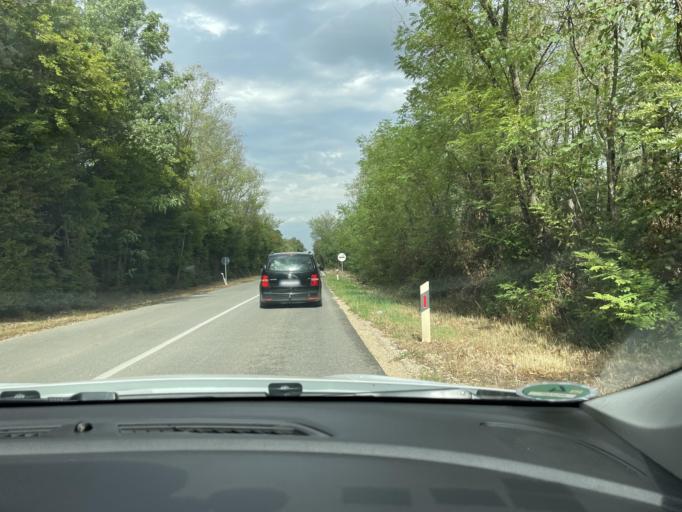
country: HR
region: Istarska
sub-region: Grad Porec
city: Porec
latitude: 45.2021
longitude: 13.6954
